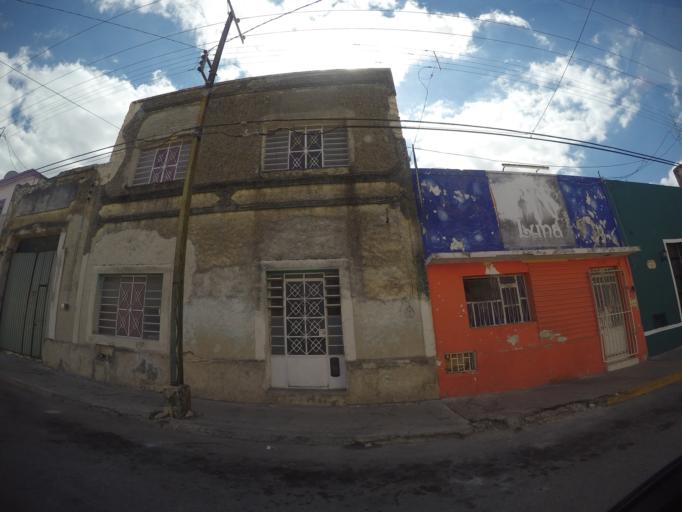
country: MX
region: Yucatan
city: Merida
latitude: 20.9763
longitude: -89.6268
